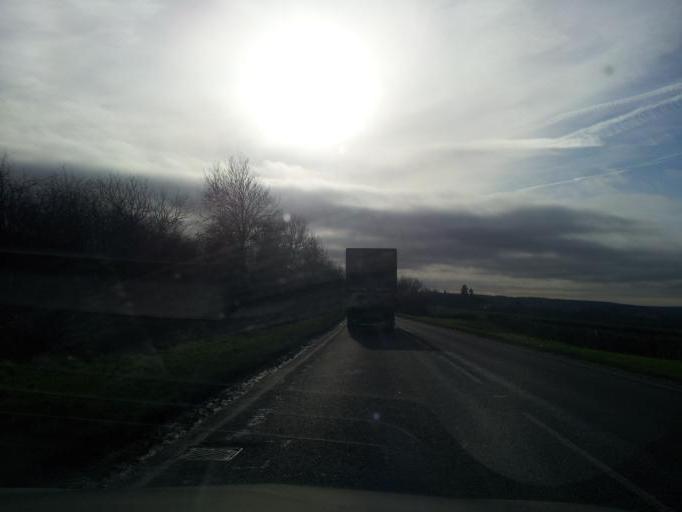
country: GB
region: England
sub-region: District of Rutland
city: Ketton
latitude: 52.6057
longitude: -0.5361
